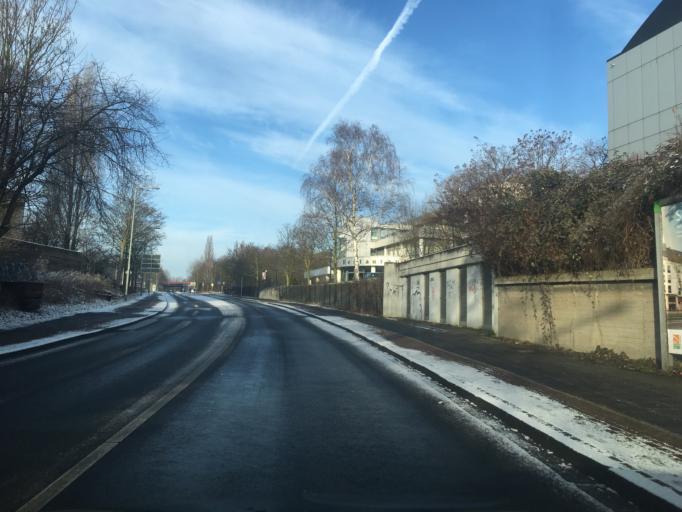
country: DE
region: North Rhine-Westphalia
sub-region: Regierungsbezirk Dusseldorf
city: Oberhausen
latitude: 51.5029
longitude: 6.8802
